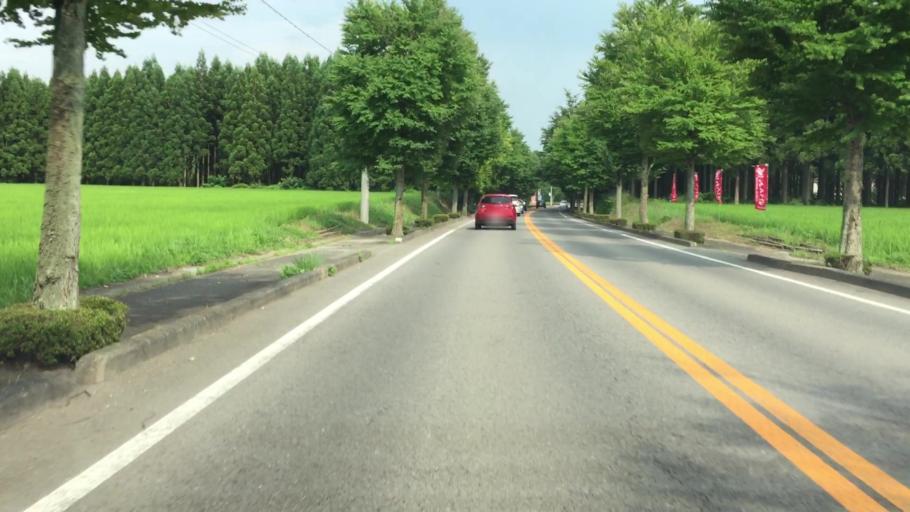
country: JP
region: Tochigi
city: Kuroiso
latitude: 36.9882
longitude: 139.9515
